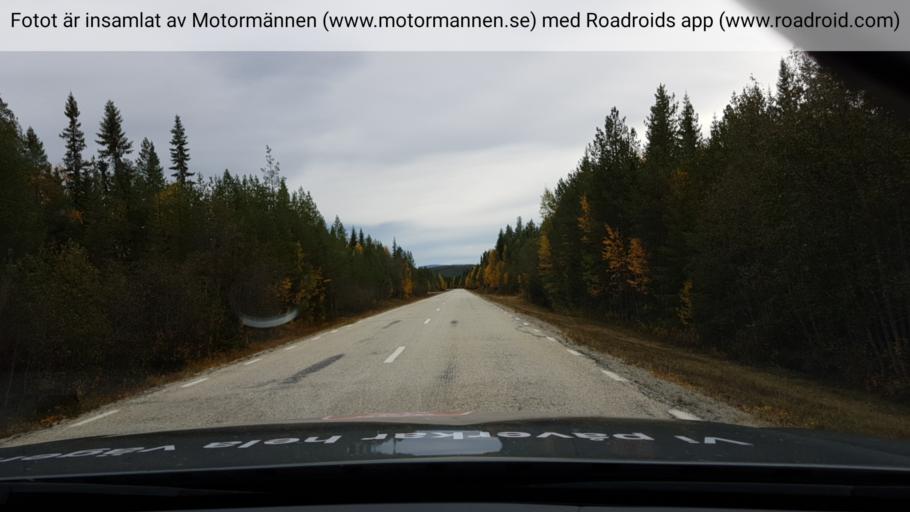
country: SE
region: Jaemtland
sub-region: Are Kommun
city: Jarpen
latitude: 62.7603
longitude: 13.7333
